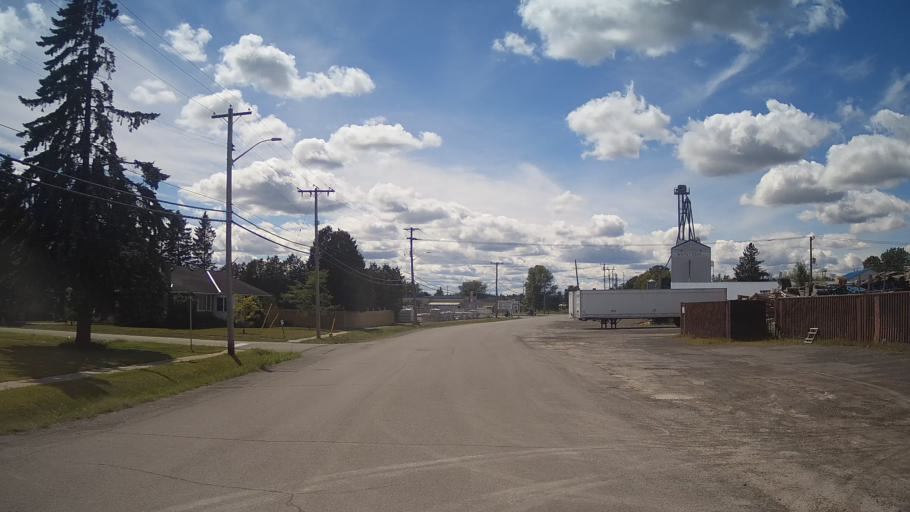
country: US
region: New York
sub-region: St. Lawrence County
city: Ogdensburg
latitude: 44.8465
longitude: -75.3193
